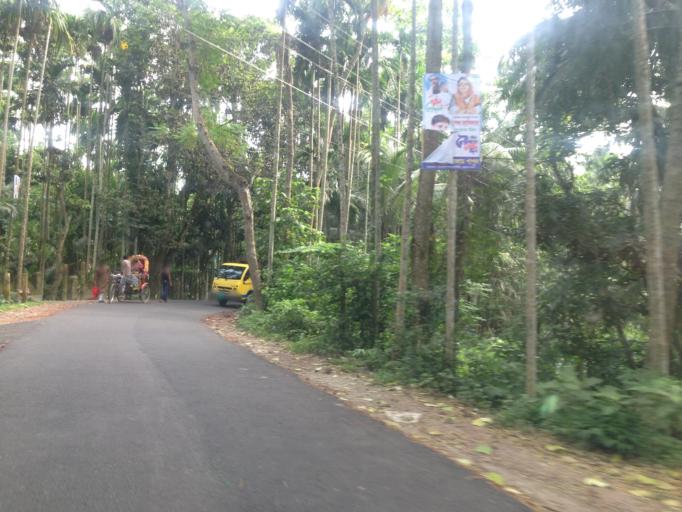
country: BD
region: Chittagong
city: Raipur
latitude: 23.0369
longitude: 90.7244
